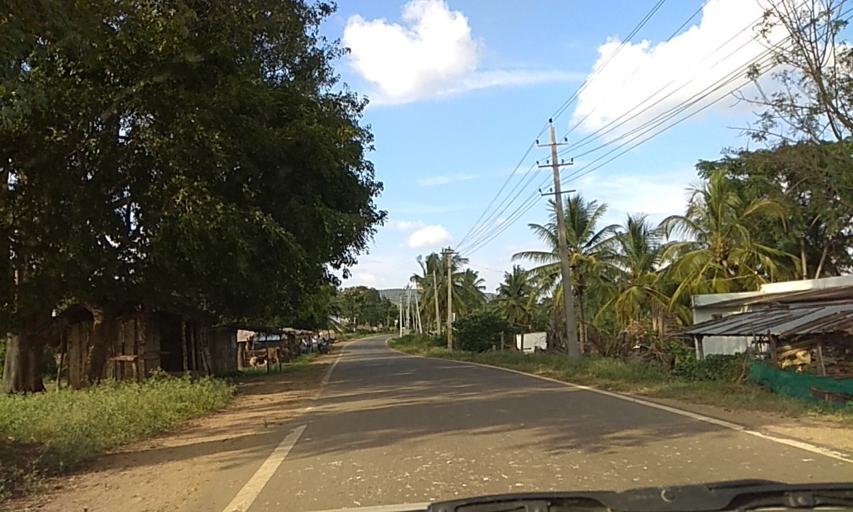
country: IN
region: Karnataka
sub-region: Chamrajnagar
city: Gundlupet
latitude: 11.7590
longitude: 76.7696
